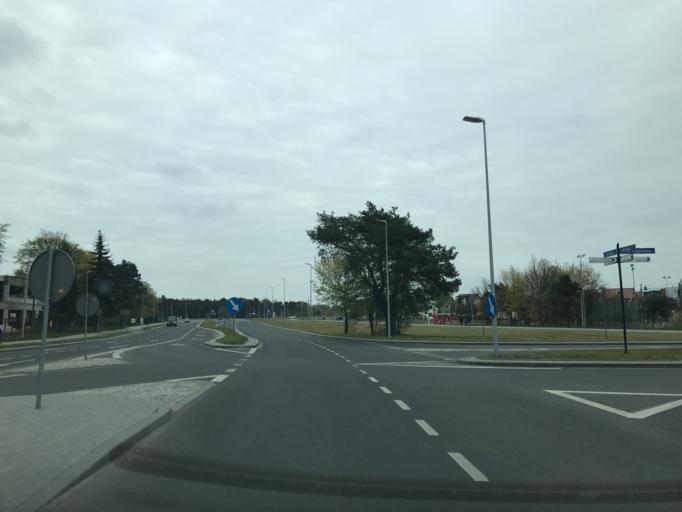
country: PL
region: Kujawsko-Pomorskie
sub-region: Torun
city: Torun
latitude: 53.0374
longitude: 18.5969
